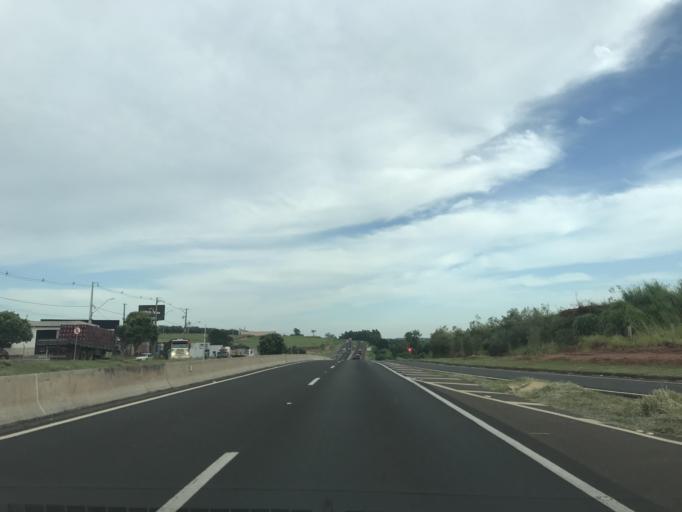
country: BR
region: Parana
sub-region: Alto Parana
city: Alto Parana
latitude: -23.1274
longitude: -52.3038
